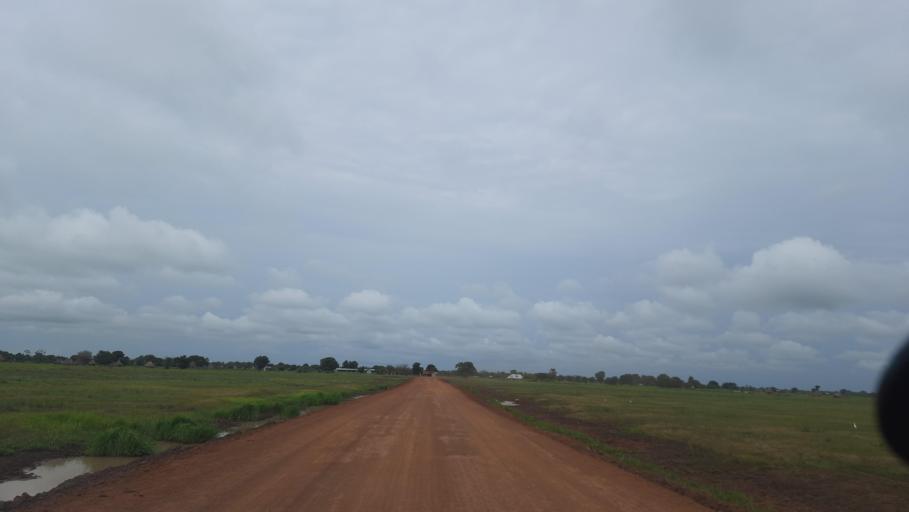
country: ET
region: Gambela
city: Gambela
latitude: 8.3335
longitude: 33.7742
